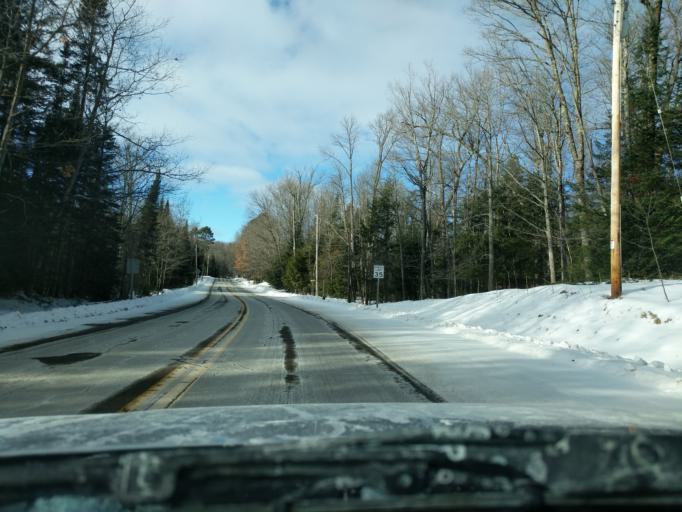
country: US
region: Wisconsin
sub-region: Vilas County
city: Eagle River
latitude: 45.7815
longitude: -89.0744
